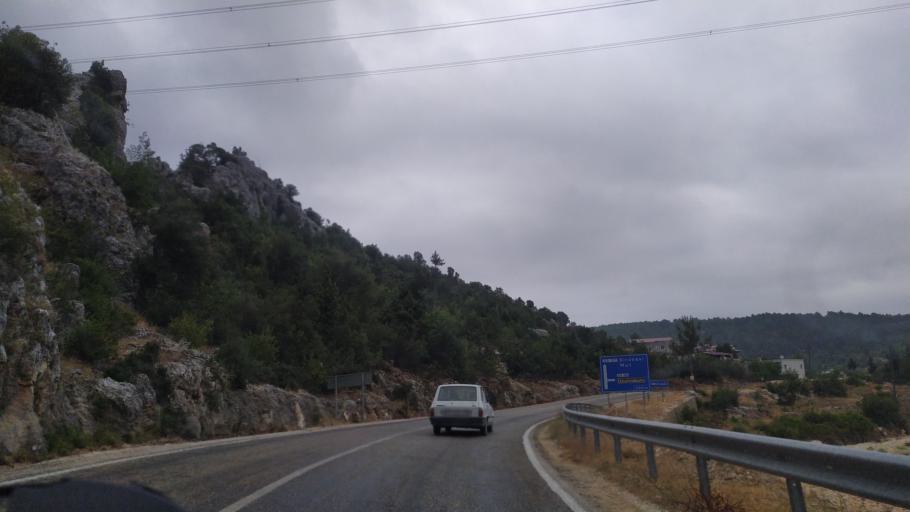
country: TR
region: Mersin
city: Silifke
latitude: 36.5342
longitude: 33.9423
